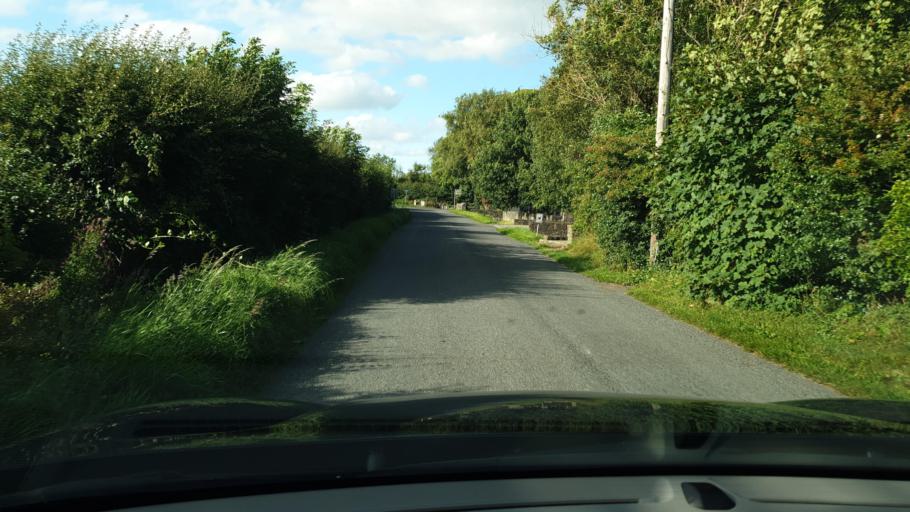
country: IE
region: Leinster
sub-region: An Mhi
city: Ashbourne
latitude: 53.5800
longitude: -6.3494
